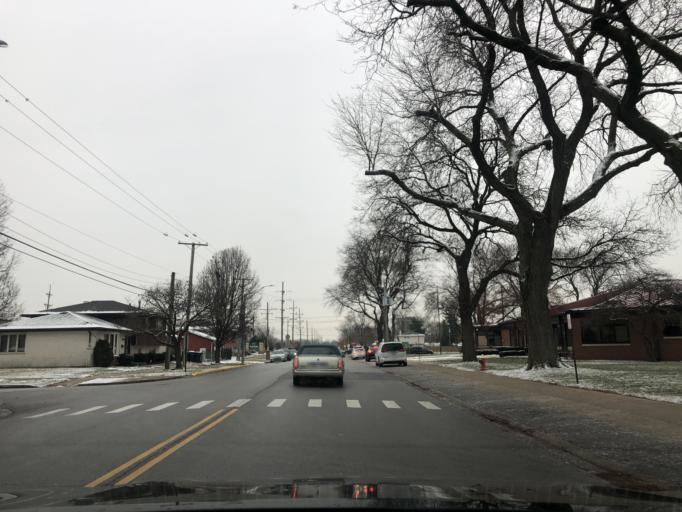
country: US
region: Illinois
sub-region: Cook County
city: Evergreen Park
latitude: 41.7293
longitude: -87.6922
